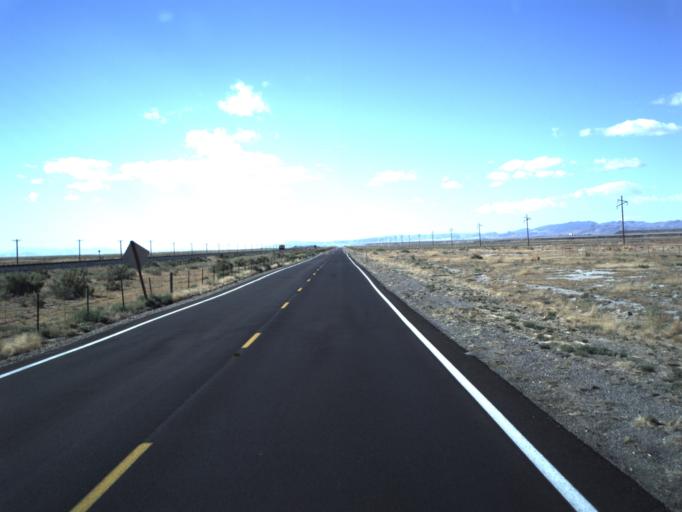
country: US
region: Utah
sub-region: Millard County
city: Delta
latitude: 39.2241
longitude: -112.6731
